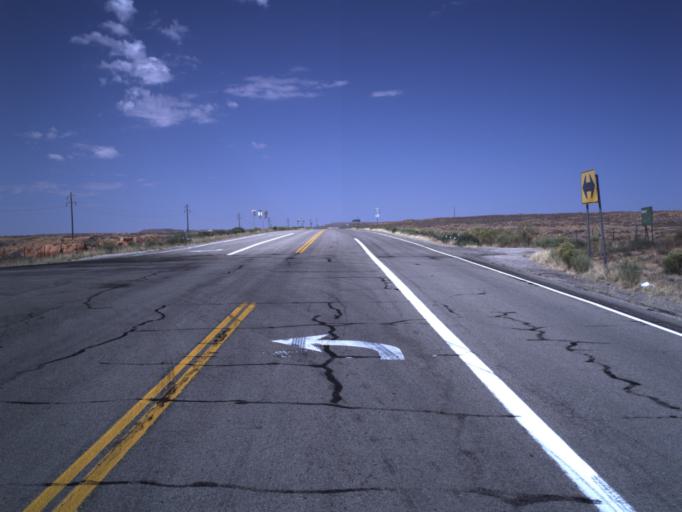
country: US
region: Utah
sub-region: San Juan County
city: Blanding
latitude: 37.2656
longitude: -109.6253
